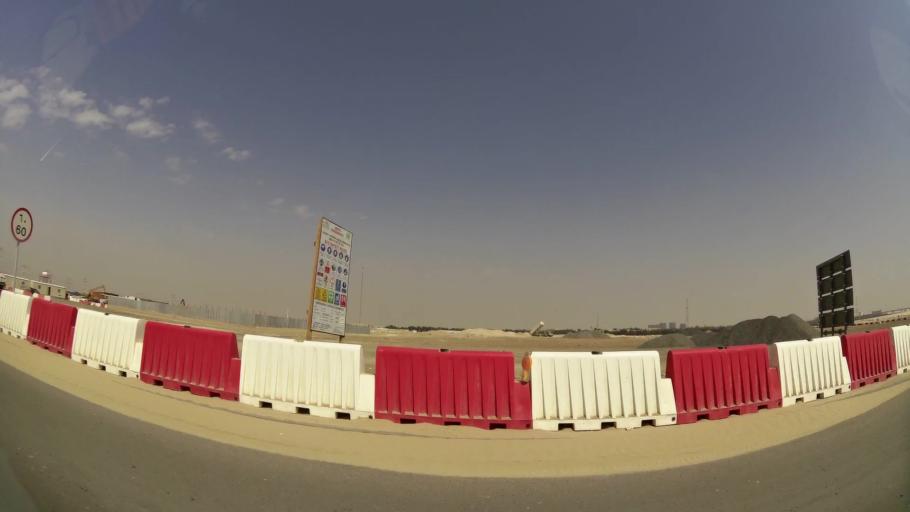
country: AE
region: Abu Dhabi
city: Abu Dhabi
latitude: 24.3154
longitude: 54.5829
